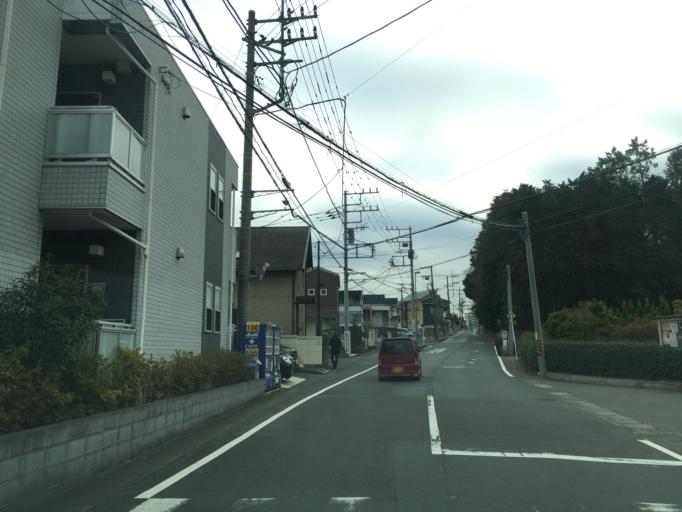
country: JP
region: Kanagawa
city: Minami-rinkan
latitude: 35.5100
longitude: 139.4639
